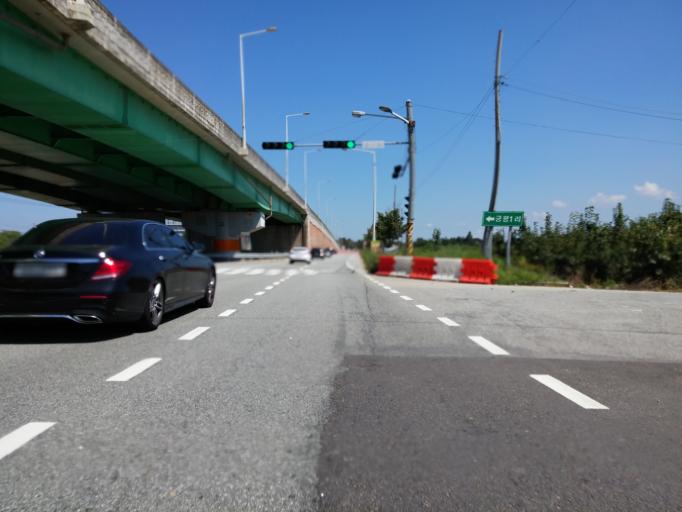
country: KR
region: Chungcheongbuk-do
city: Cheongju-si
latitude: 36.6191
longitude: 127.3414
